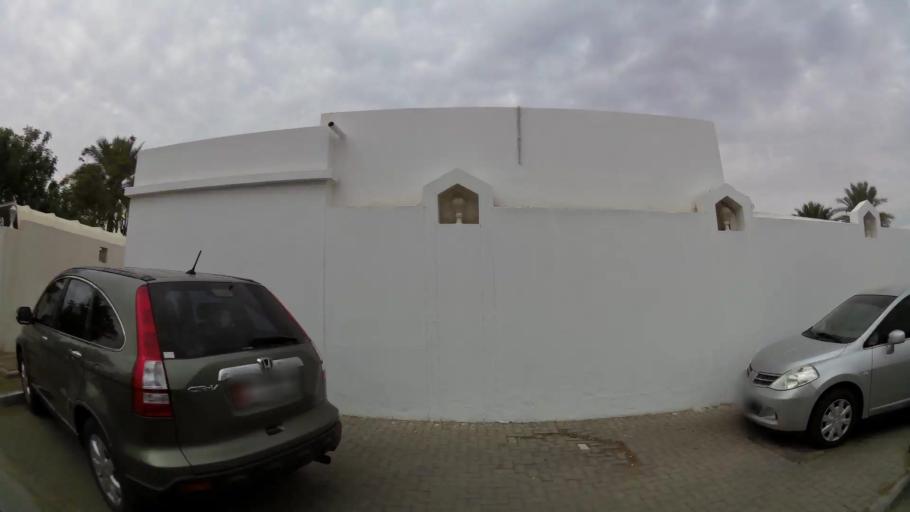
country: AE
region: Abu Dhabi
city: Al Ain
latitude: 24.2274
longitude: 55.7433
